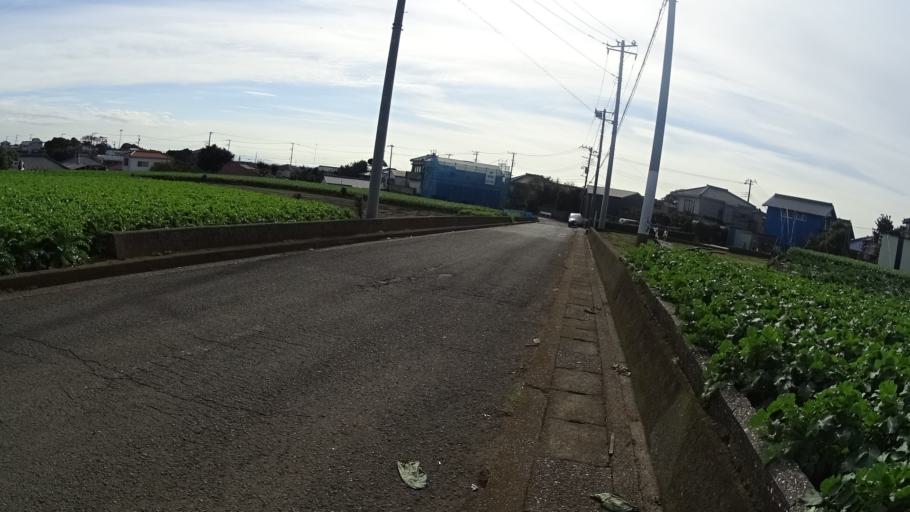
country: JP
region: Kanagawa
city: Miura
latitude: 35.1516
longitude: 139.6714
